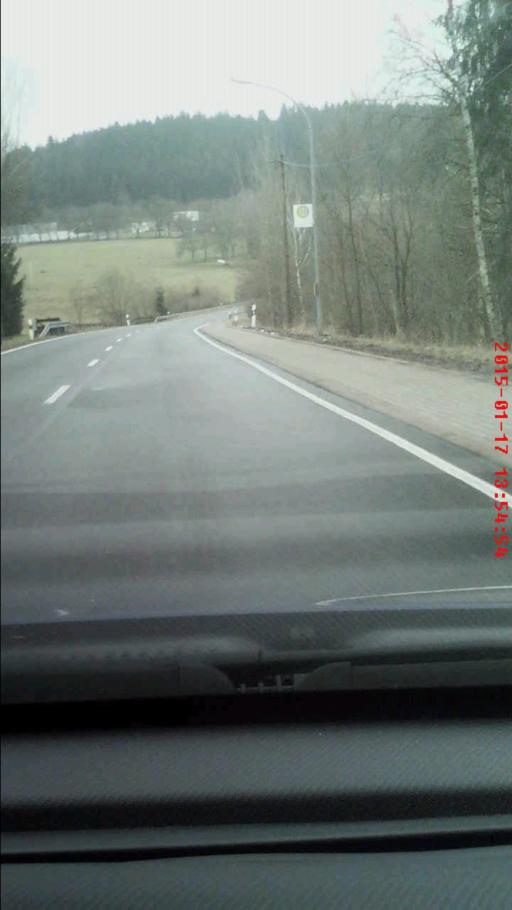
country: DE
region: Thuringia
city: Steinheid
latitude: 50.4925
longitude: 11.0612
